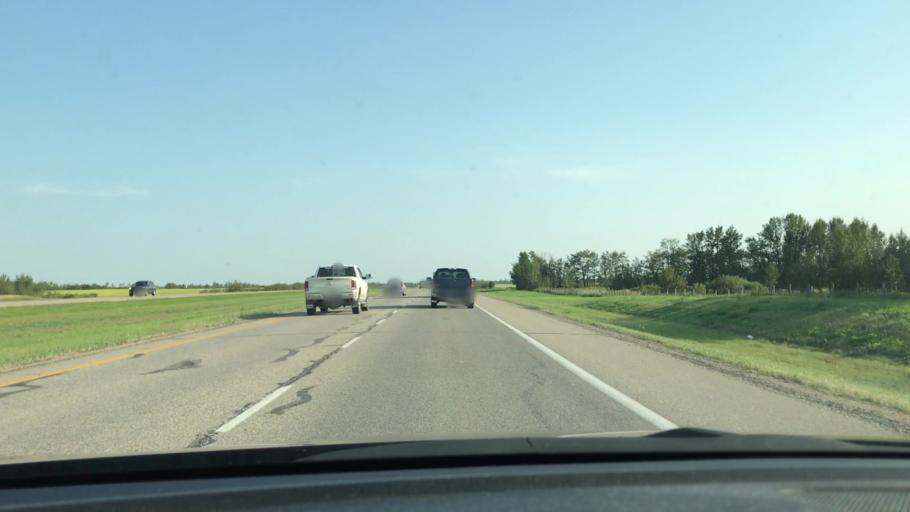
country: CA
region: Alberta
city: Millet
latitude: 53.0712
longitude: -113.5983
